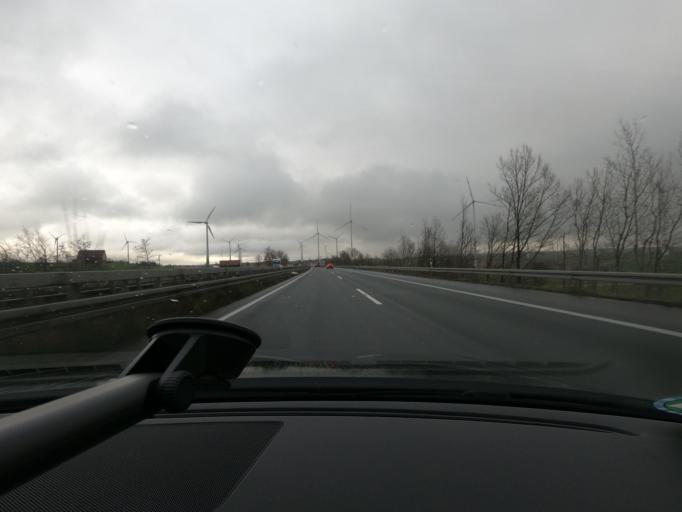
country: DE
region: North Rhine-Westphalia
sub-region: Regierungsbezirk Detmold
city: Wunnenberg
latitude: 51.5599
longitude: 8.7626
